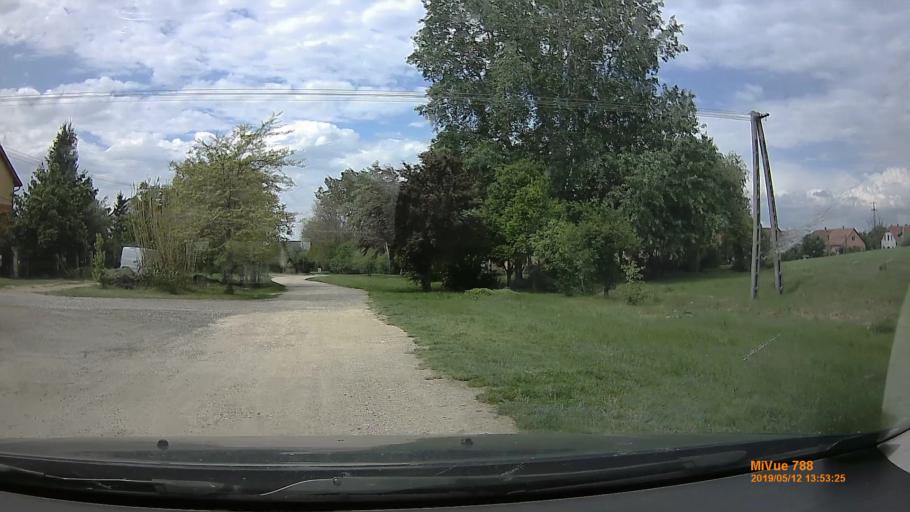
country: HU
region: Pest
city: Pecel
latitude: 47.4878
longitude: 19.2991
